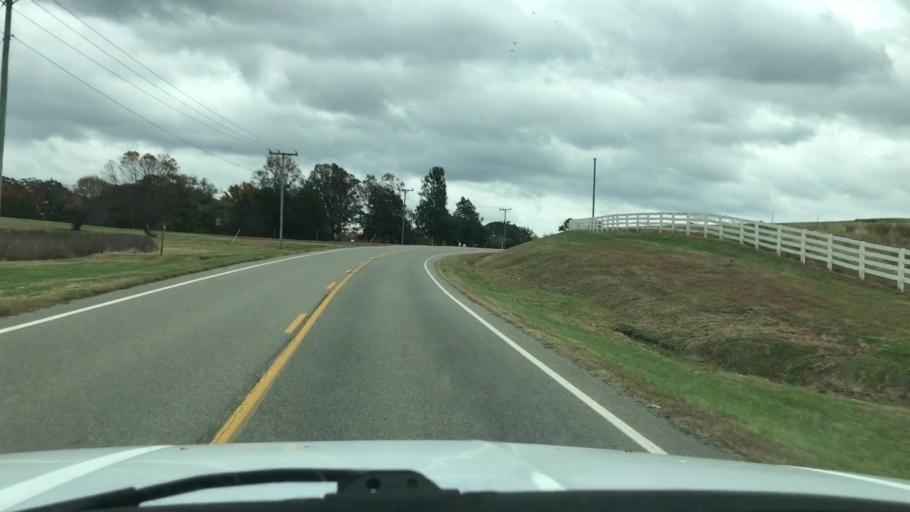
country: US
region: Virginia
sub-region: Goochland County
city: Goochland
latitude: 37.6462
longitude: -77.8203
